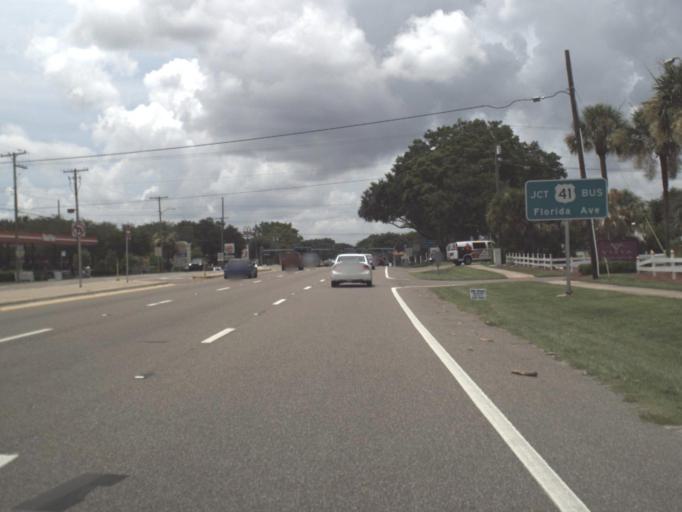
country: US
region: Florida
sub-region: Hillsborough County
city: Lake Magdalene
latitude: 28.0881
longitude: -82.4567
